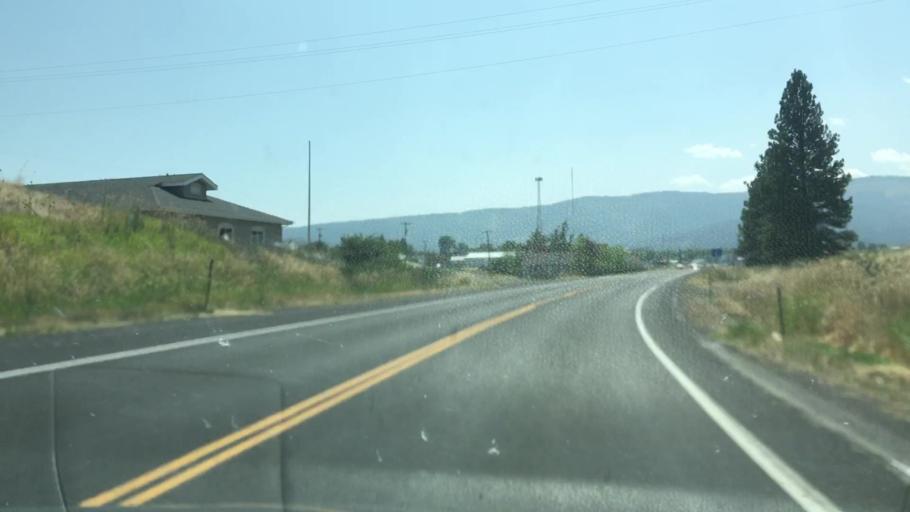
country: US
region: Idaho
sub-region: Idaho County
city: Grangeville
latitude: 45.9344
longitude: -116.1332
